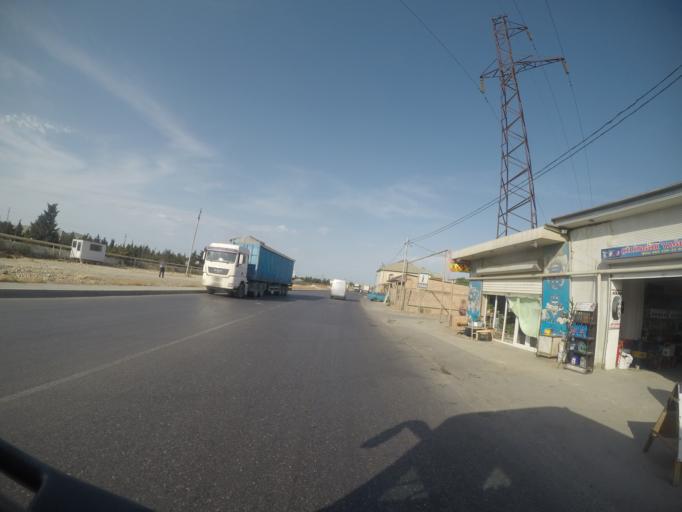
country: AZ
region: Baki
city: Bilajari
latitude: 40.4425
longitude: 49.7870
